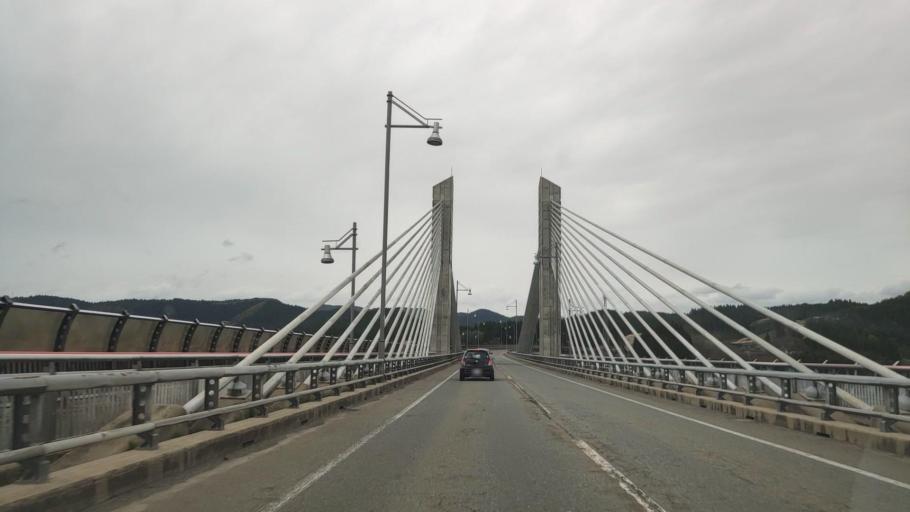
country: JP
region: Akita
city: Takanosu
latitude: 40.2074
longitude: 140.3034
